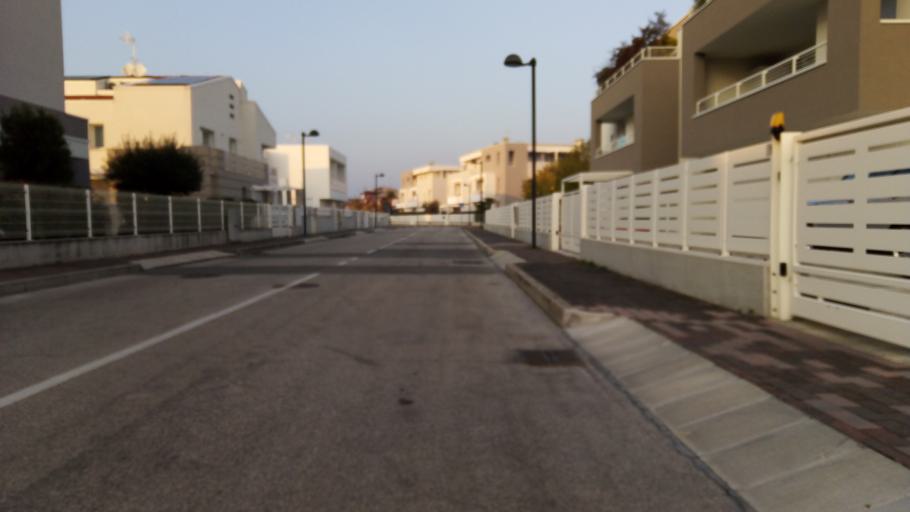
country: IT
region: Veneto
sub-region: Provincia di Padova
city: Abano Terme
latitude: 45.3531
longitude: 11.7679
